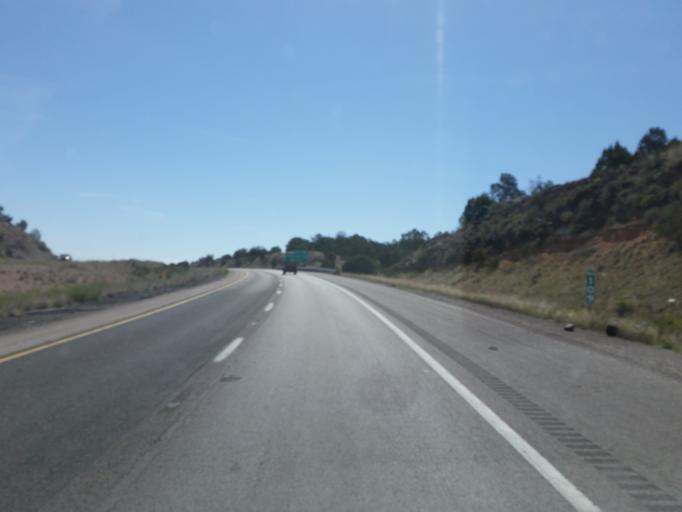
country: US
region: Arizona
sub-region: Mohave County
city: Peach Springs
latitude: 35.2855
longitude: -113.0976
